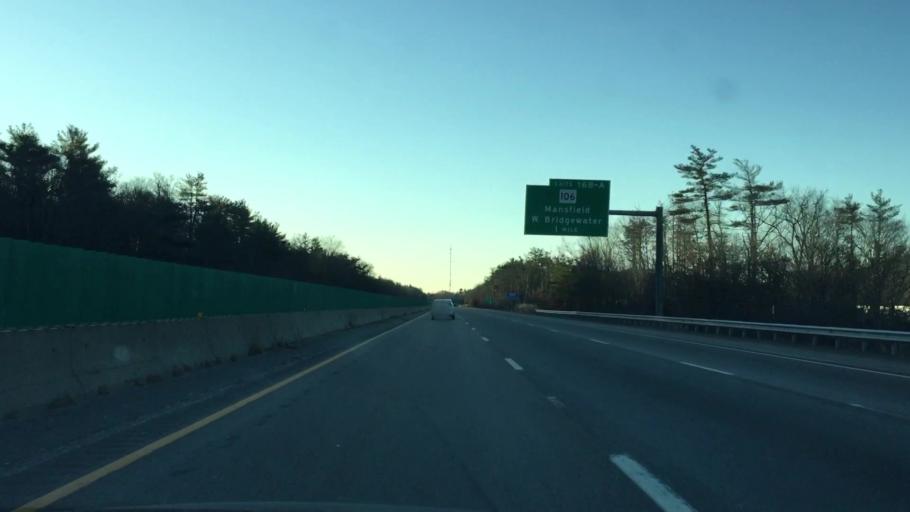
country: US
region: Massachusetts
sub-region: Plymouth County
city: West Bridgewater
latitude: 42.0324
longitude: -71.0518
